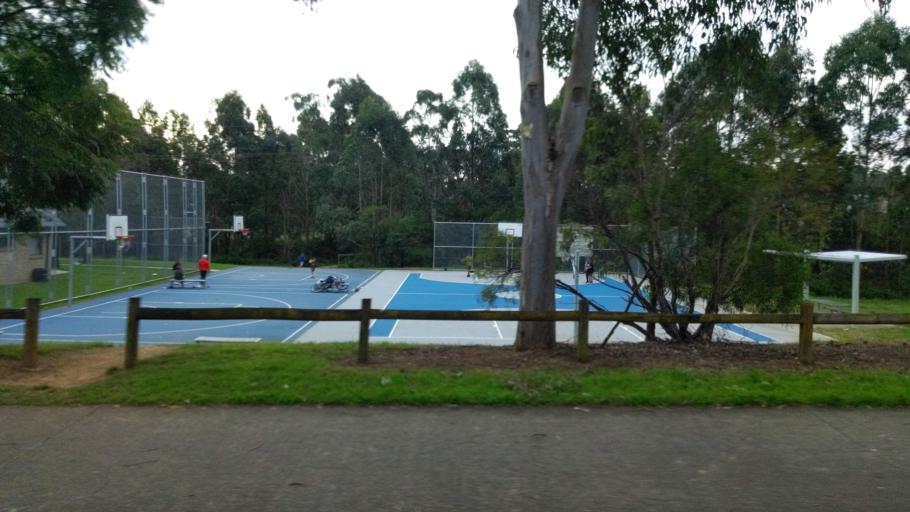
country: AU
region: New South Wales
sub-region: Blacktown
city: Blacktown
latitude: -33.7540
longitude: 150.9433
